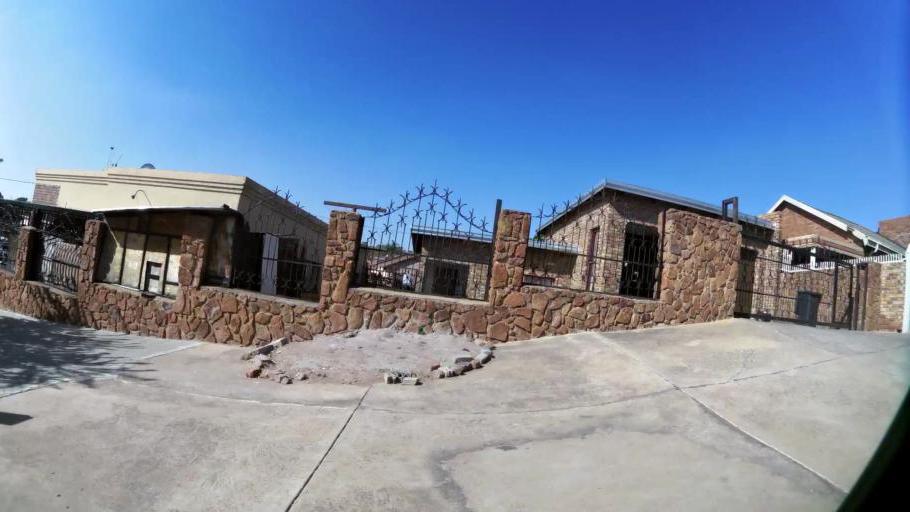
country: ZA
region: Gauteng
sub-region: City of Tshwane Metropolitan Municipality
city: Mabopane
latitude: -25.5321
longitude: 28.0894
